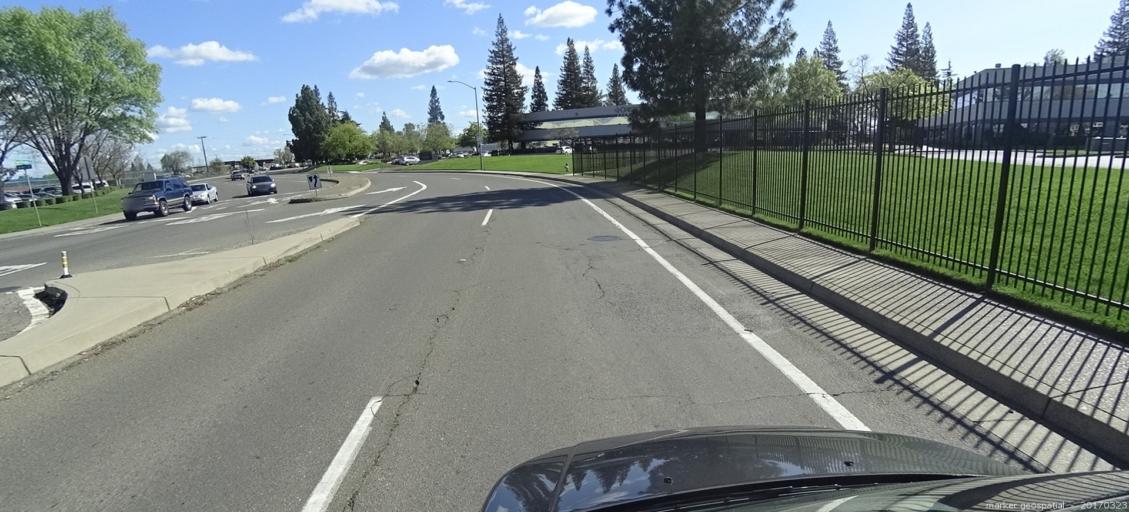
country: US
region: California
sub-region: Sacramento County
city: Rosemont
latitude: 38.5467
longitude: -121.3923
